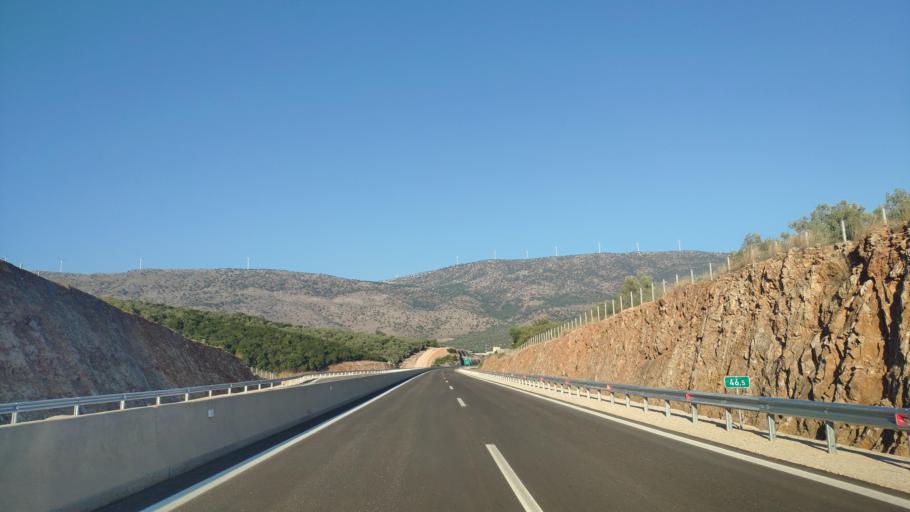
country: GR
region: West Greece
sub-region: Nomos Aitolias kai Akarnanias
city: Stanos
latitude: 38.7717
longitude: 21.1658
